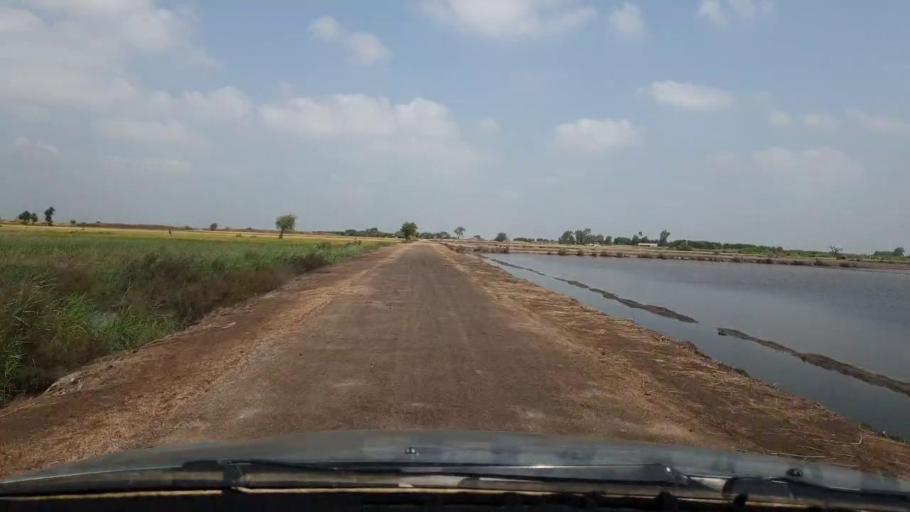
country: PK
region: Sindh
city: Matli
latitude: 25.0896
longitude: 68.6915
